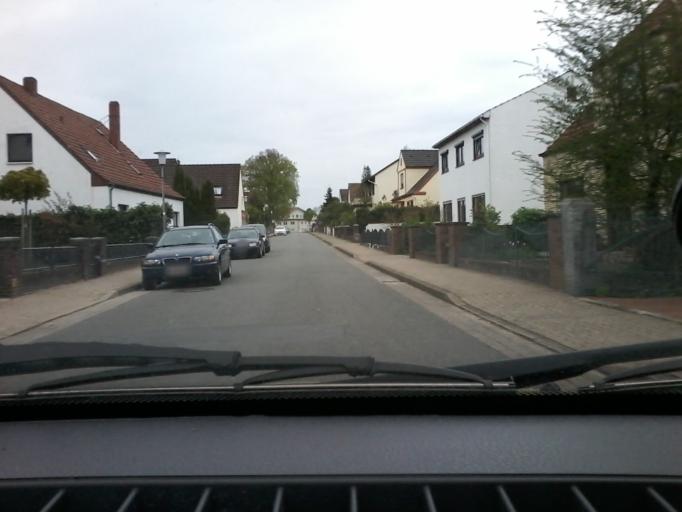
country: DE
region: Lower Saxony
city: Achim
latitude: 53.0028
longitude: 9.0472
